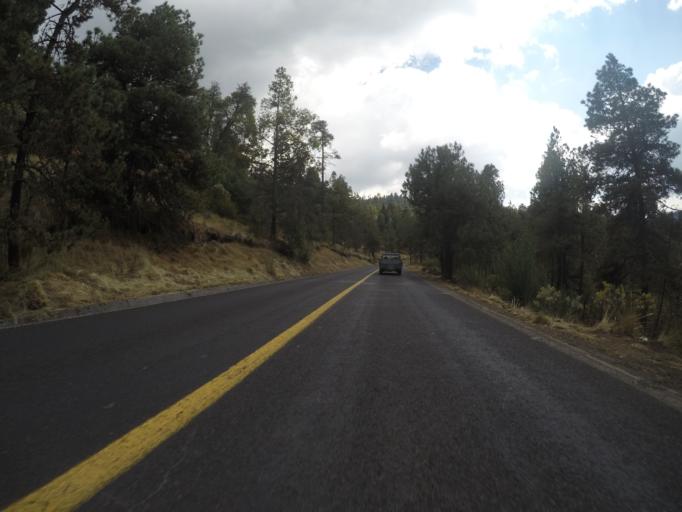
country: MX
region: Mexico
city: Cerro La Calera
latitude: 19.1420
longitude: -99.8039
